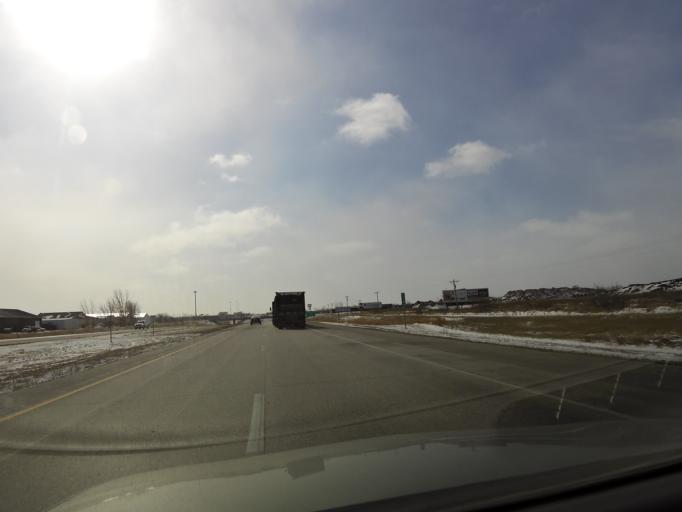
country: US
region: North Dakota
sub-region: Grand Forks County
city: Grand Forks
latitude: 47.9451
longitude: -97.0938
